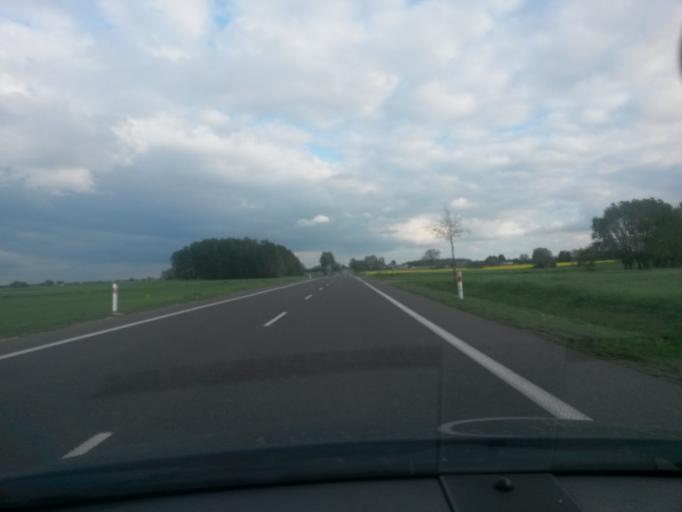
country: PL
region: Masovian Voivodeship
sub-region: Powiat plocki
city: Drobin
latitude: 52.6998
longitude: 20.0402
